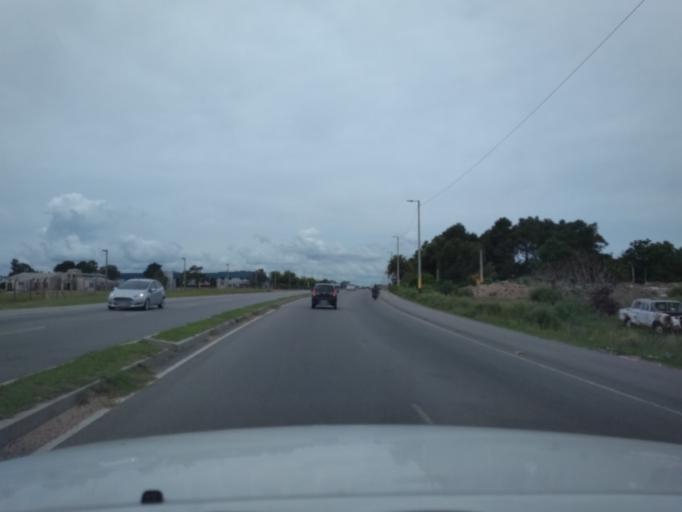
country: UY
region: Canelones
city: Paso de Carrasco
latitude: -34.8481
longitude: -56.0316
